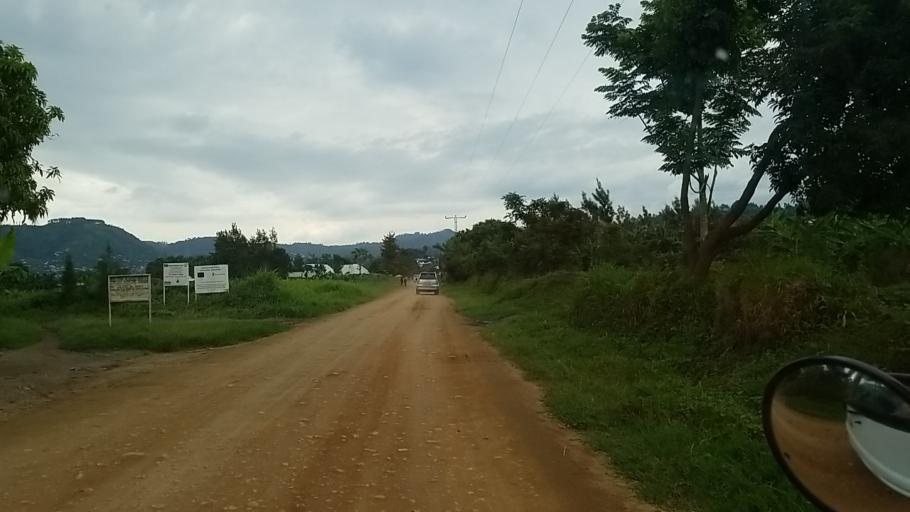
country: CD
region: Nord Kivu
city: Sake
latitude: -1.6831
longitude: 29.0162
